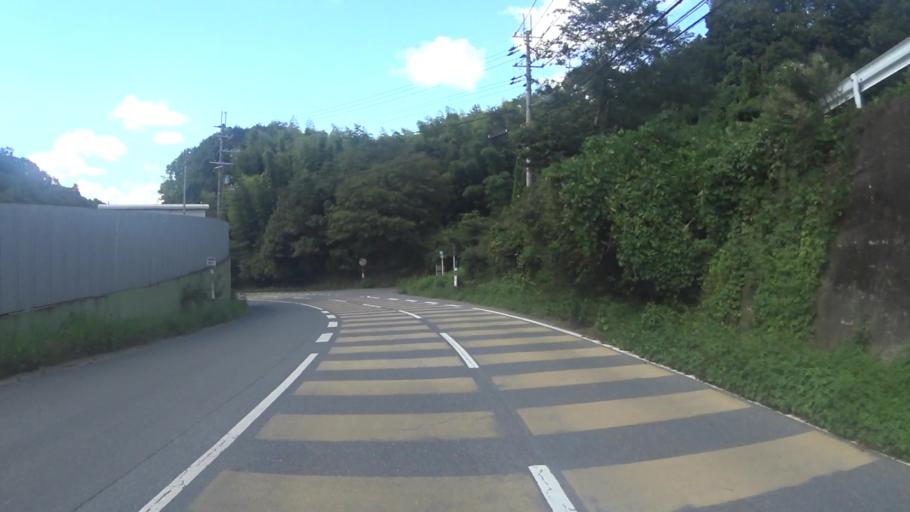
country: JP
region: Nara
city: Nara-shi
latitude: 34.7112
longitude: 135.8867
